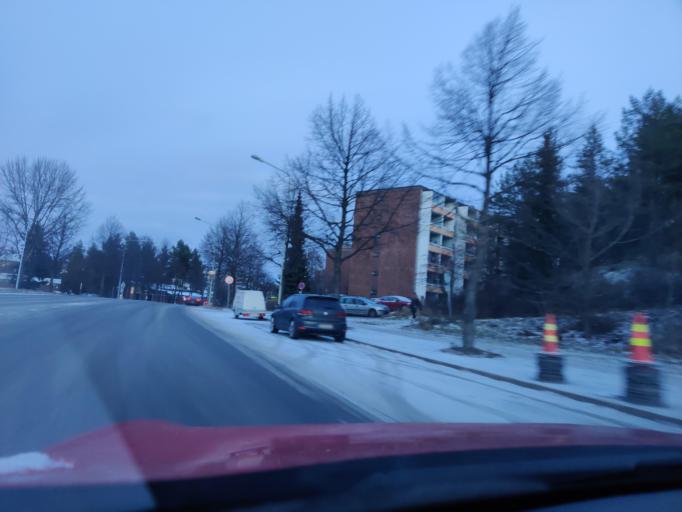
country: FI
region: Pirkanmaa
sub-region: Tampere
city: Nokia
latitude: 61.4775
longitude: 23.5140
